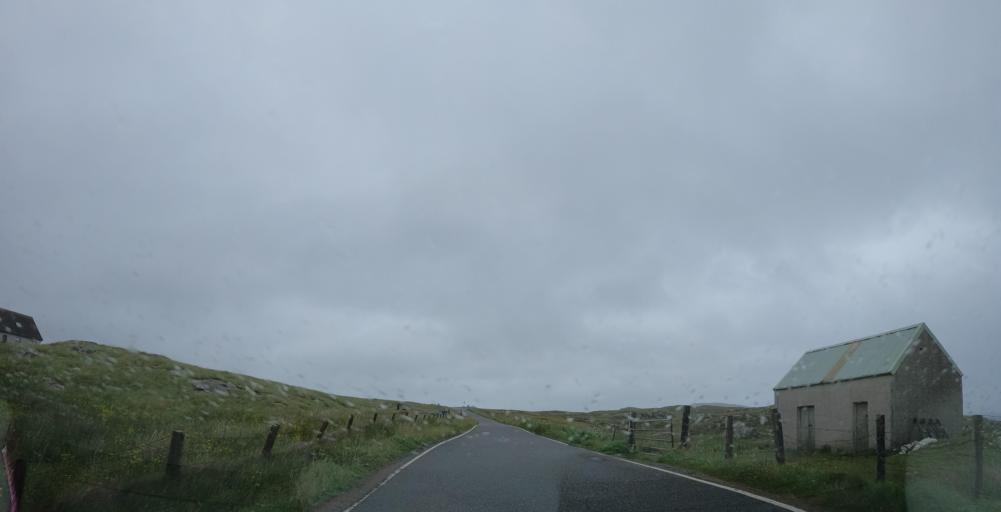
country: GB
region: Scotland
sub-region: Eilean Siar
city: Barra
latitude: 56.9775
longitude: -7.4187
